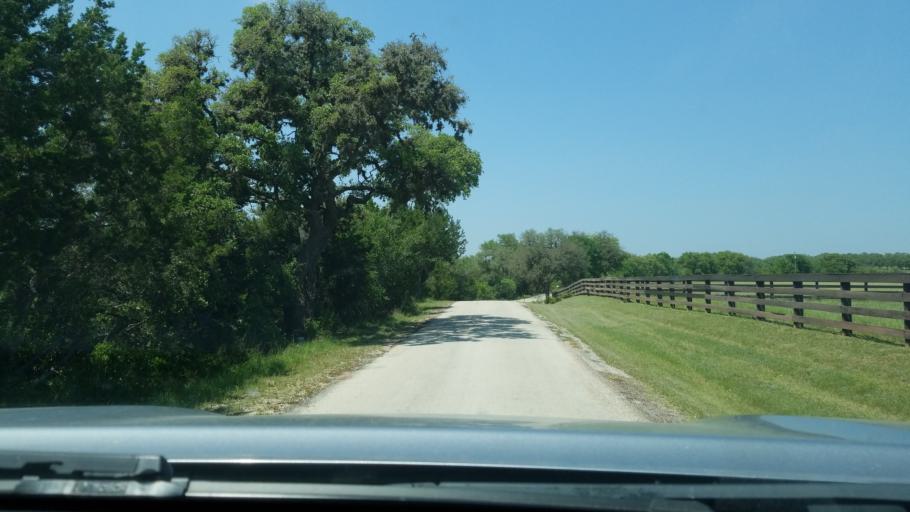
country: US
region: Texas
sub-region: Blanco County
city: Blanco
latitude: 30.0084
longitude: -98.4364
